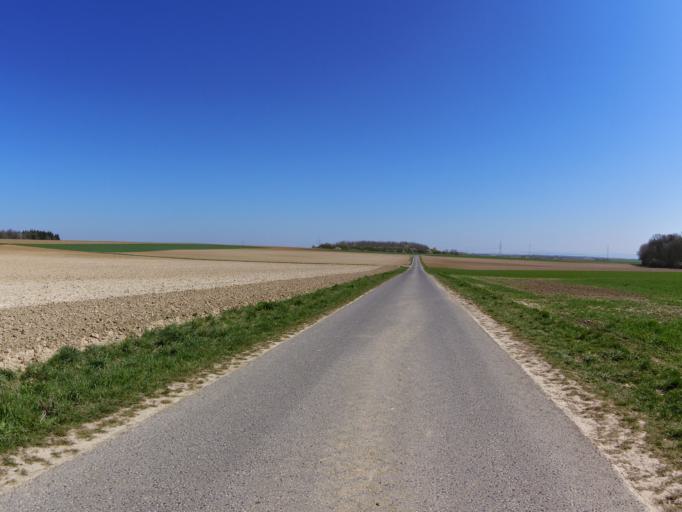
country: DE
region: Bavaria
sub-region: Regierungsbezirk Unterfranken
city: Kurnach
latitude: 49.8357
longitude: 10.0643
